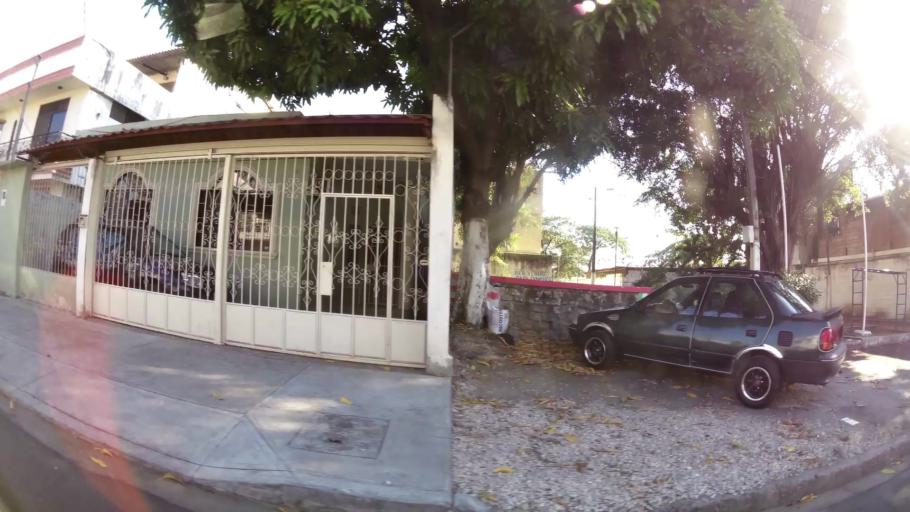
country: EC
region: Guayas
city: Eloy Alfaro
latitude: -2.1671
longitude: -79.8863
